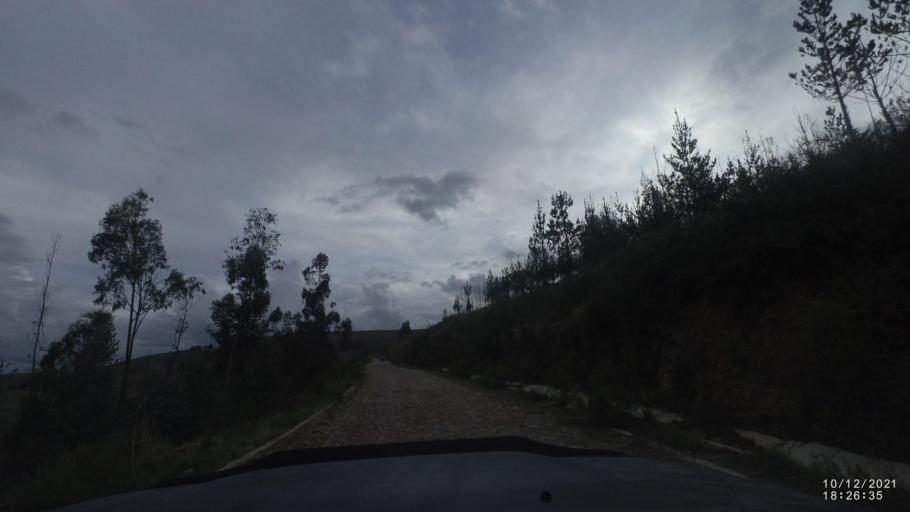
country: BO
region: Cochabamba
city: Tarata
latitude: -17.7976
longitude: -65.9739
